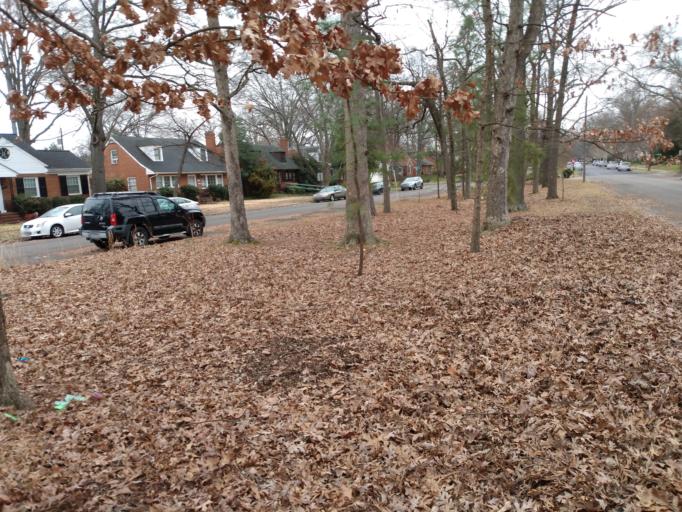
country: US
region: Virginia
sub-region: Henrico County
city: Dumbarton
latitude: 37.5741
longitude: -77.4964
